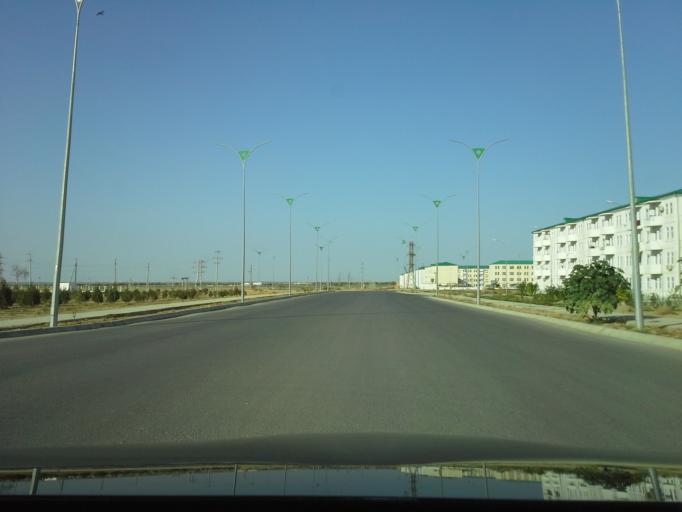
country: TM
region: Ahal
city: Abadan
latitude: 38.0555
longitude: 58.1381
